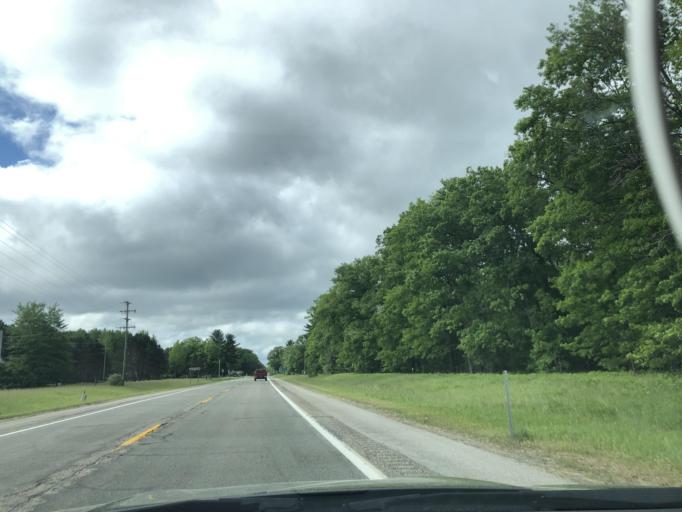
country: US
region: Michigan
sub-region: Missaukee County
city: Lake City
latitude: 44.3708
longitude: -85.2164
